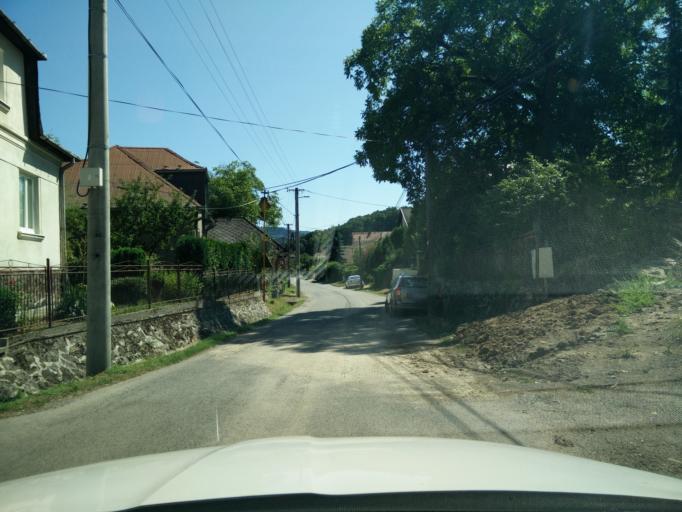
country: SK
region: Nitriansky
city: Prievidza
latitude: 48.7969
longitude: 18.6998
